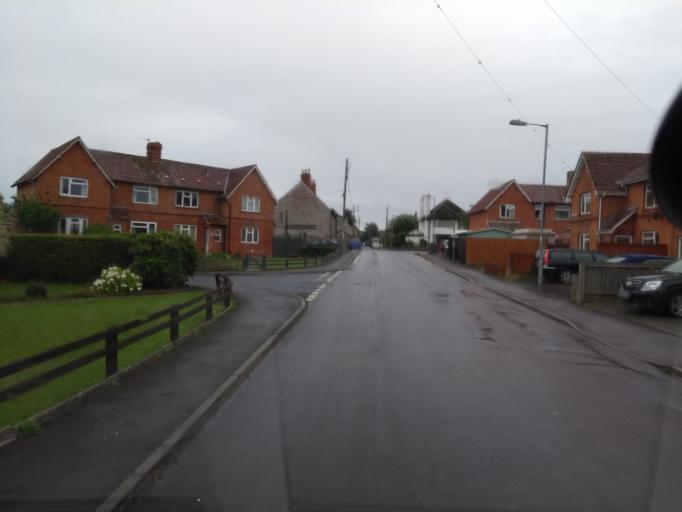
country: GB
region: England
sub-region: Somerset
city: Street
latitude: 51.1192
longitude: -2.7410
